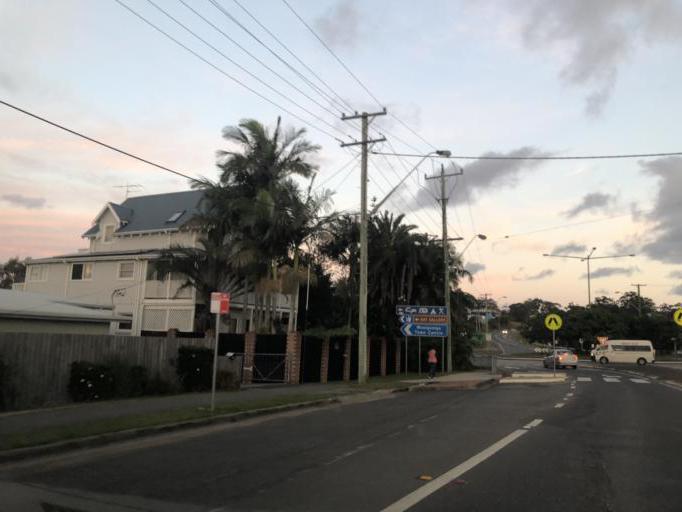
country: AU
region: New South Wales
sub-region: Coffs Harbour
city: Woolgoolga
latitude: -30.1122
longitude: 153.1905
